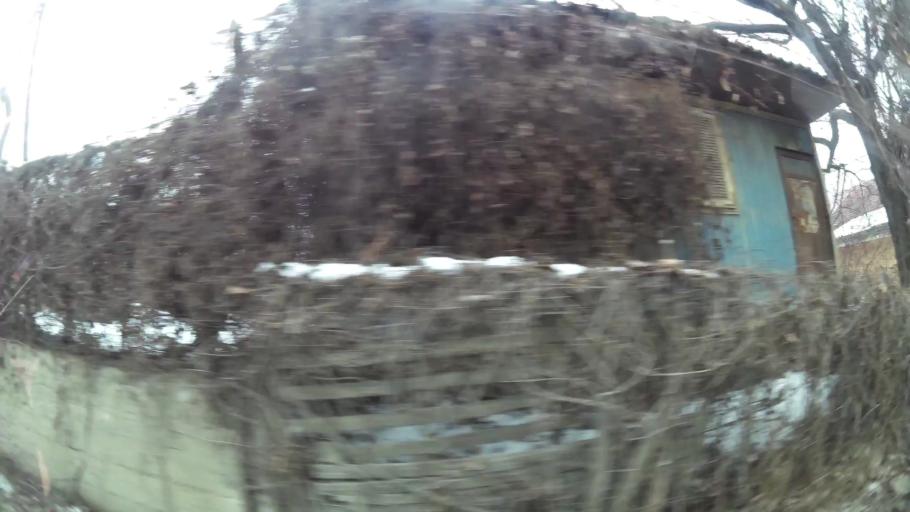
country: MK
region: Saraj
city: Saraj
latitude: 42.0353
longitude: 21.3485
